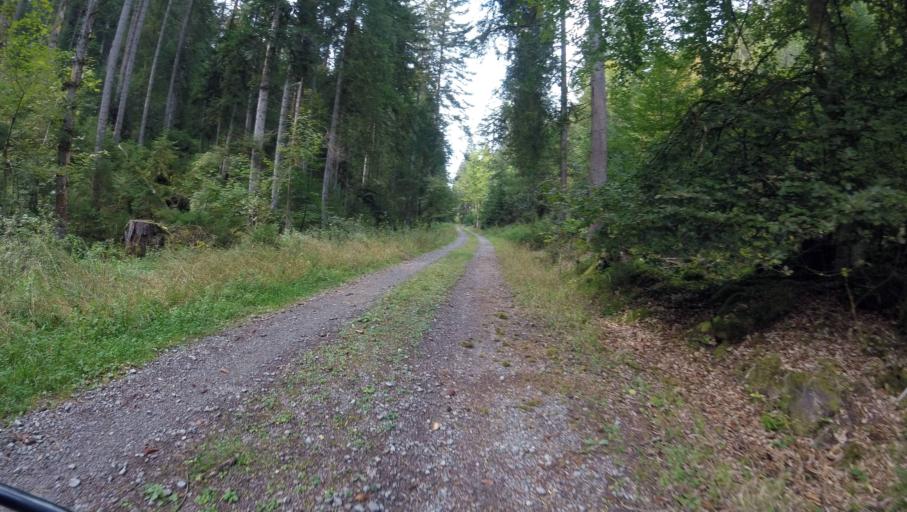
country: DE
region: Baden-Wuerttemberg
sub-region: Karlsruhe Region
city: Simmersfeld
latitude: 48.5920
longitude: 8.5167
